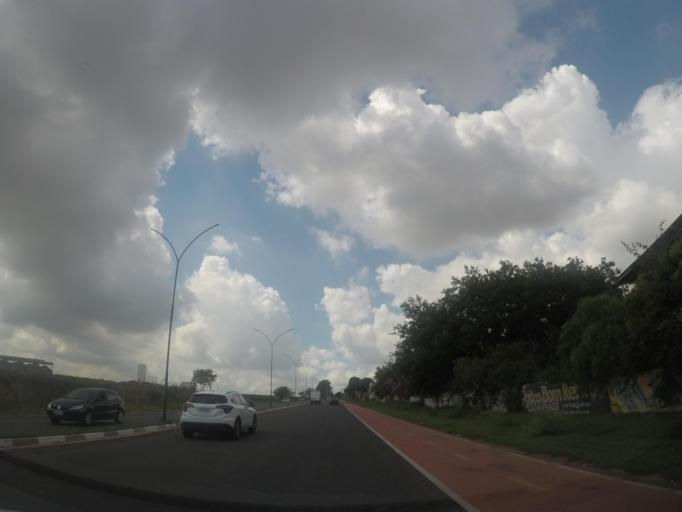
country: BR
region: Sao Paulo
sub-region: Hortolandia
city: Hortolandia
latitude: -22.8501
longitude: -47.1791
